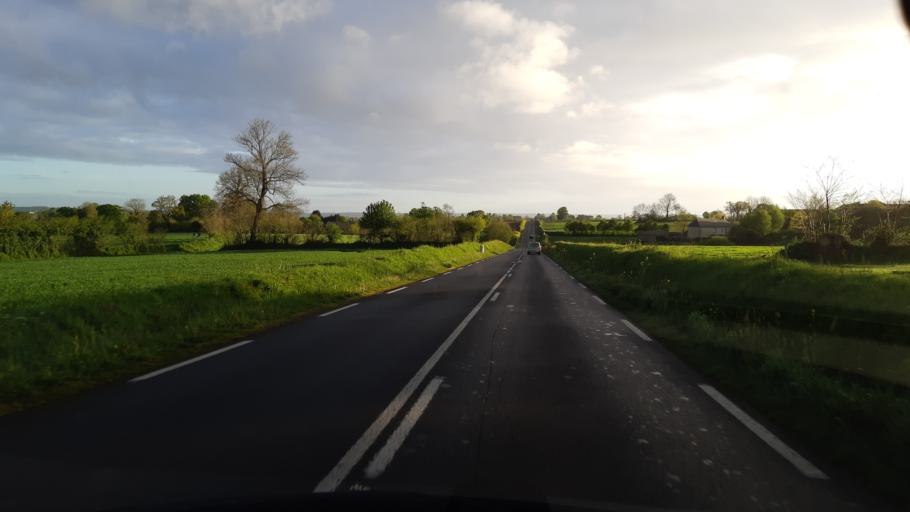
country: FR
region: Lower Normandy
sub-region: Departement de la Manche
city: Agneaux
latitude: 49.0338
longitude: -1.1349
